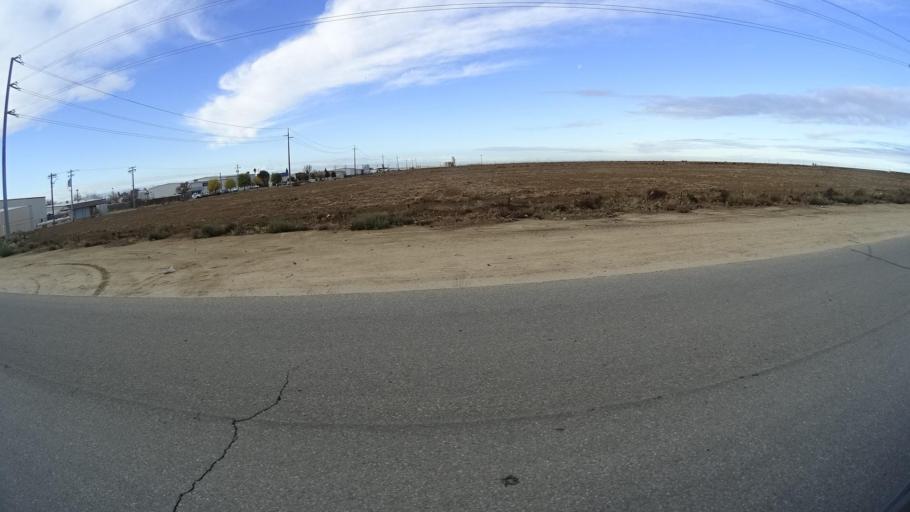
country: US
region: California
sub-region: Kern County
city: Oildale
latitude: 35.4493
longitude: -119.0823
